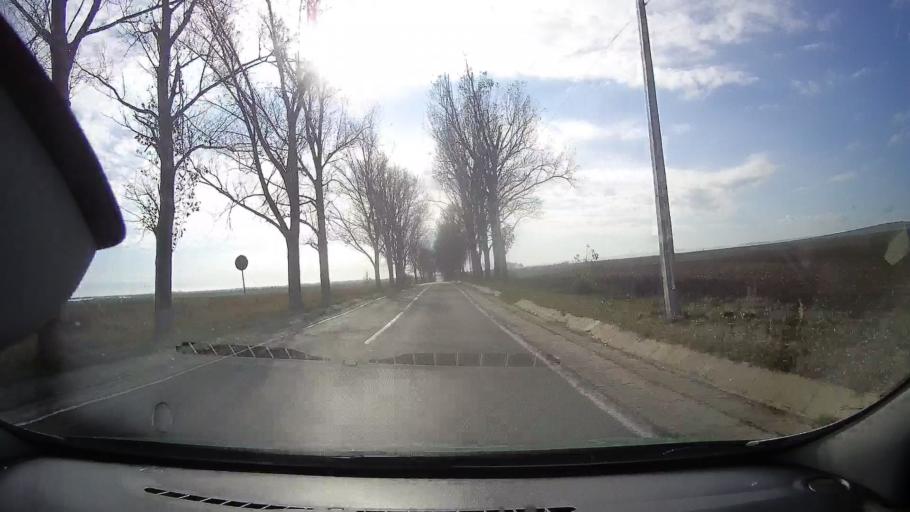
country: RO
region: Tulcea
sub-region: Comuna Valea Nucarilor
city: Agighiol
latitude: 45.0048
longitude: 28.8853
